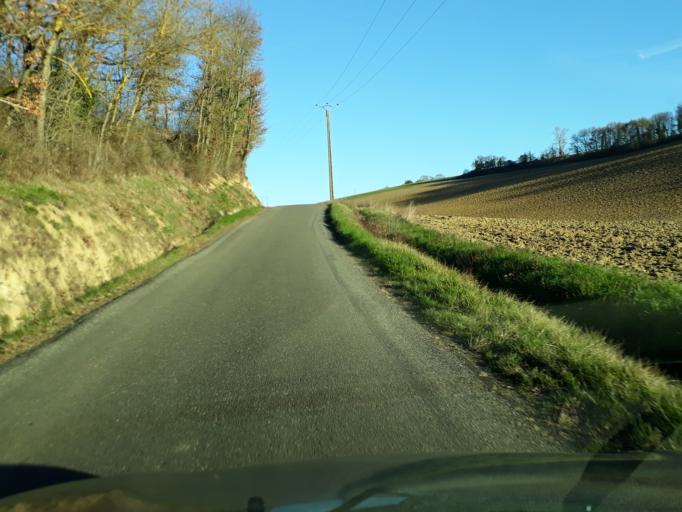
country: FR
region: Midi-Pyrenees
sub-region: Departement du Gers
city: Pavie
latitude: 43.6296
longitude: 0.6784
